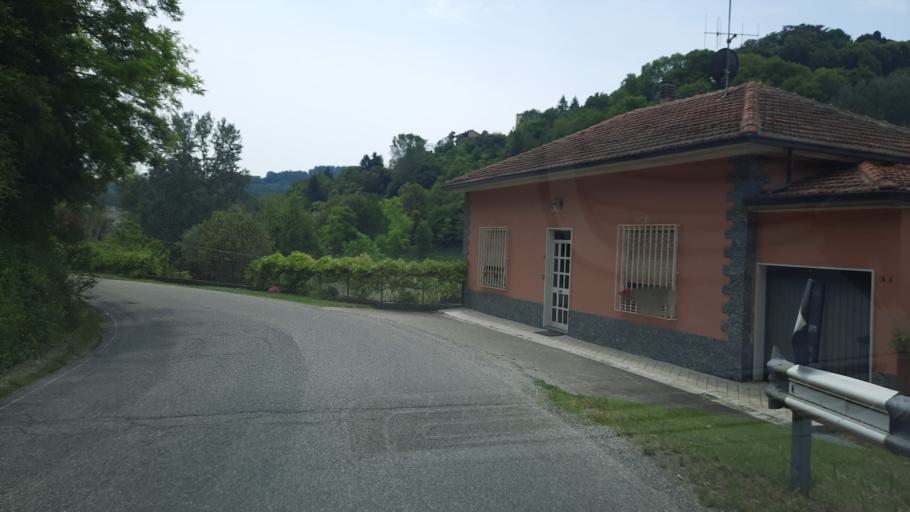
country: IT
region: Piedmont
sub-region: Provincia di Alessandria
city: Ozzano Monferrato
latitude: 45.1066
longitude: 8.3782
